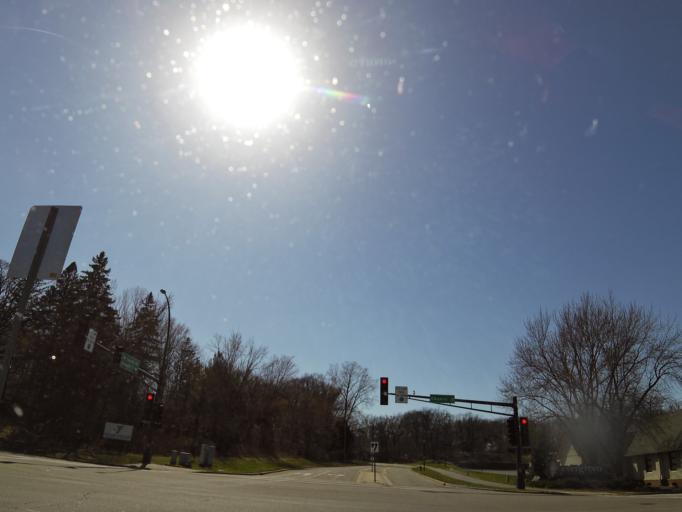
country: US
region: Minnesota
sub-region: Dakota County
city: Burnsville
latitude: 44.7147
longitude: -93.2966
